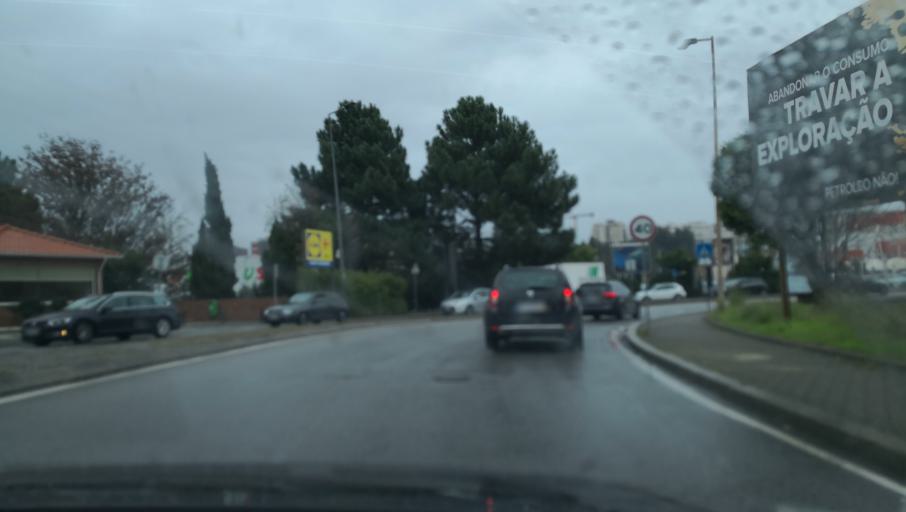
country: PT
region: Porto
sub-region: Vila Nova de Gaia
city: Vila Nova de Gaia
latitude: 41.1193
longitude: -8.6232
